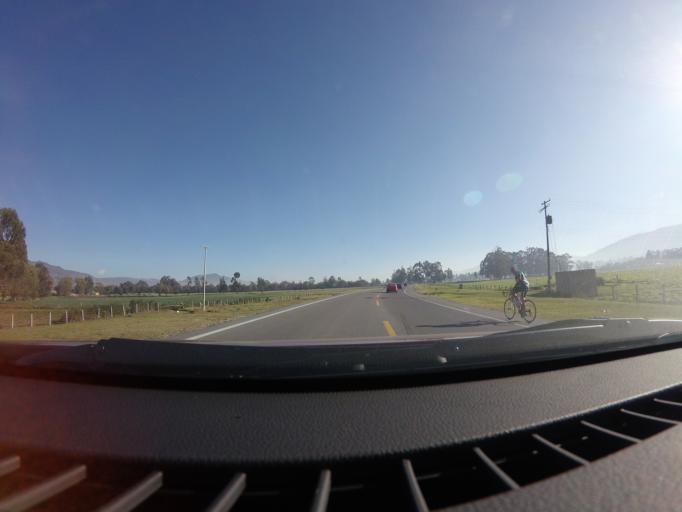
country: CO
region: Cundinamarca
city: Zipaquira
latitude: 5.0138
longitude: -73.9809
